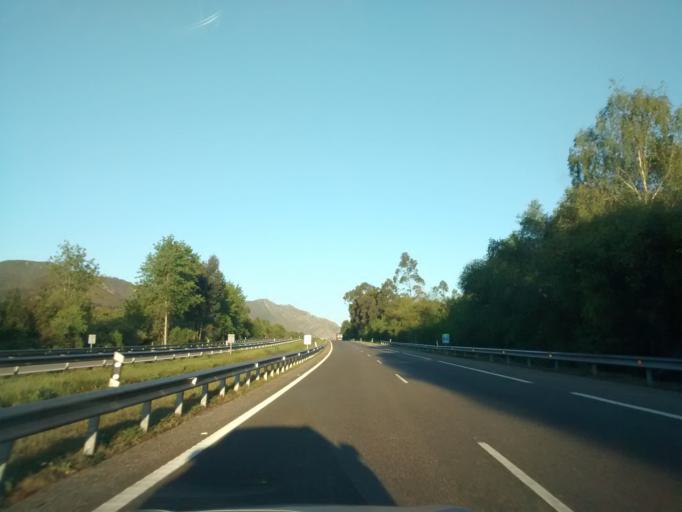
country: ES
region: Asturias
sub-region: Province of Asturias
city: Ribadesella
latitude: 43.4454
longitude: -4.9237
